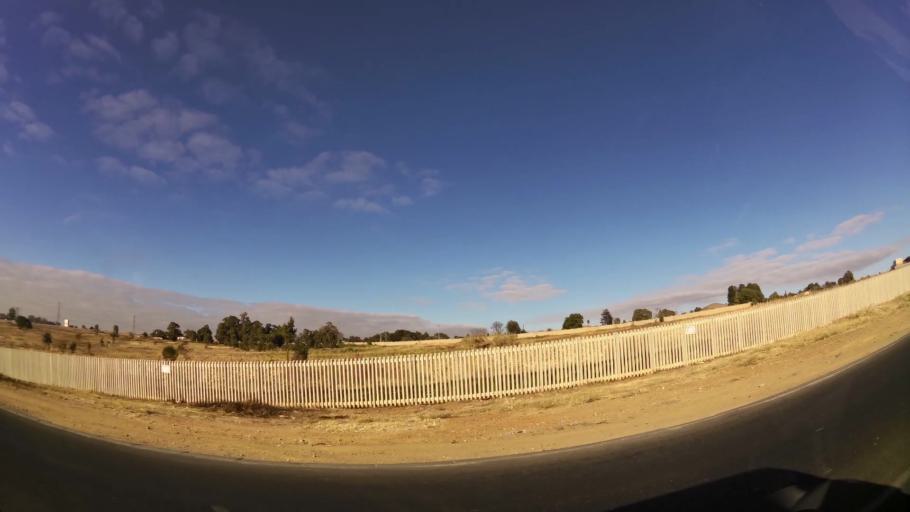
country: ZA
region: Gauteng
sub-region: City of Johannesburg Metropolitan Municipality
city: Modderfontein
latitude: -26.0540
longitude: 28.1798
